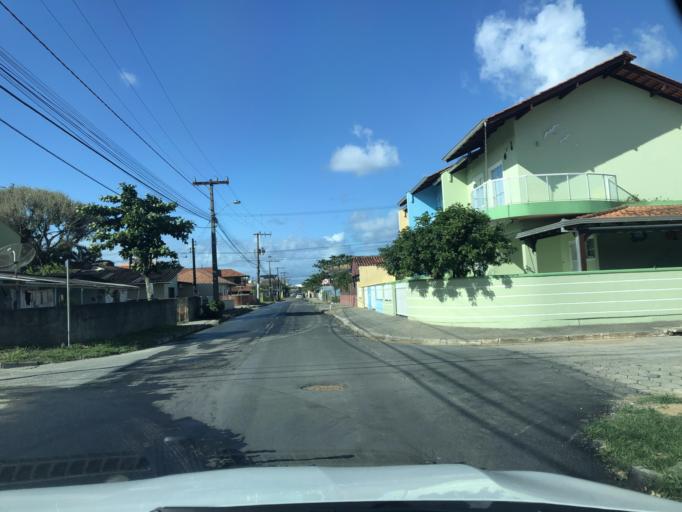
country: BR
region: Santa Catarina
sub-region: Sao Francisco Do Sul
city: Sao Francisco do Sul
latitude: -26.2329
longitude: -48.5055
